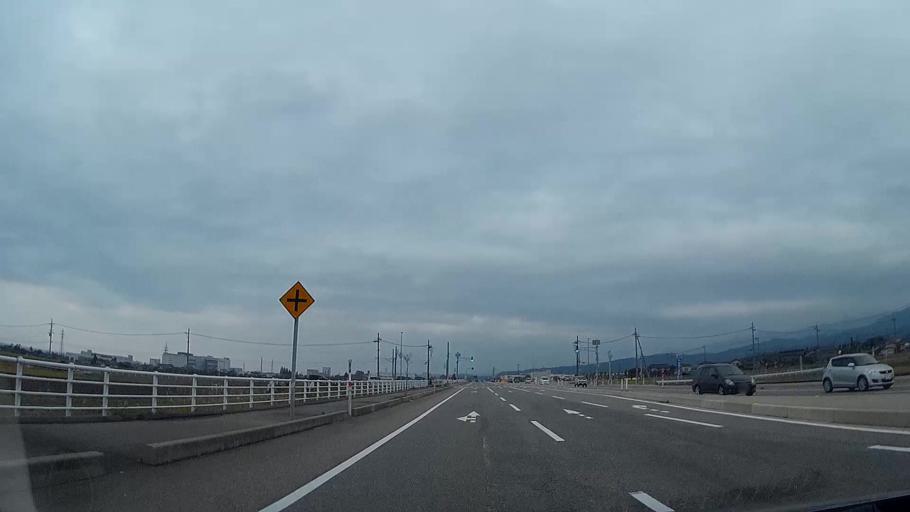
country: JP
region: Toyama
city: Uozu
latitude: 36.7727
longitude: 137.3859
